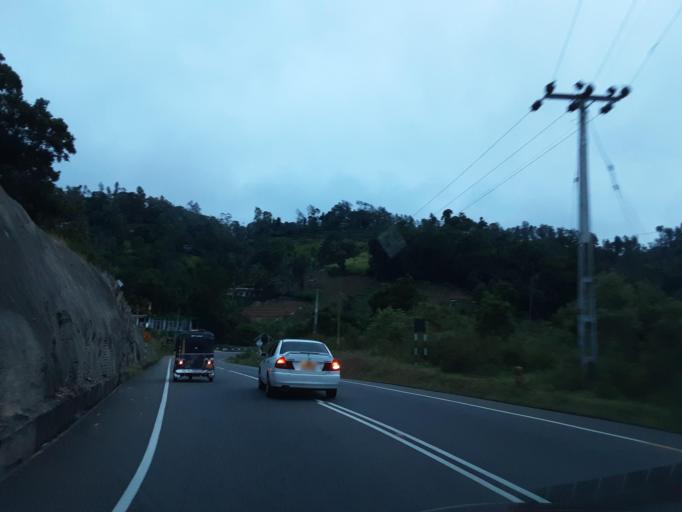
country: LK
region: Uva
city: Haputale
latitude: 6.9118
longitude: 80.9314
